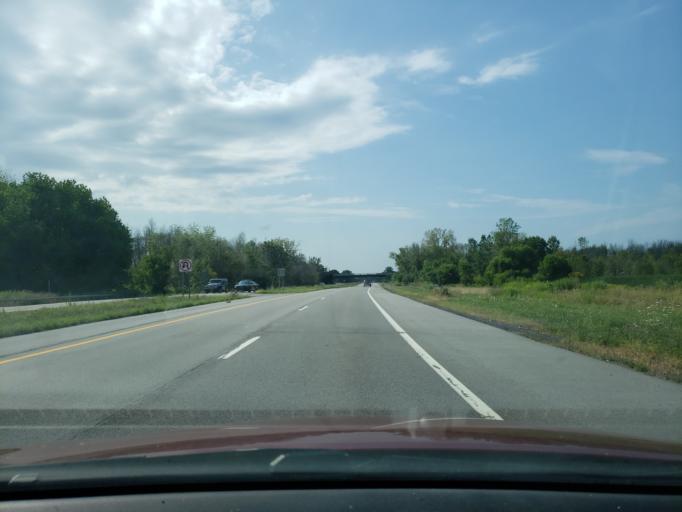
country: US
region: New York
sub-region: Monroe County
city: Greece
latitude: 43.2654
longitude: -77.6575
